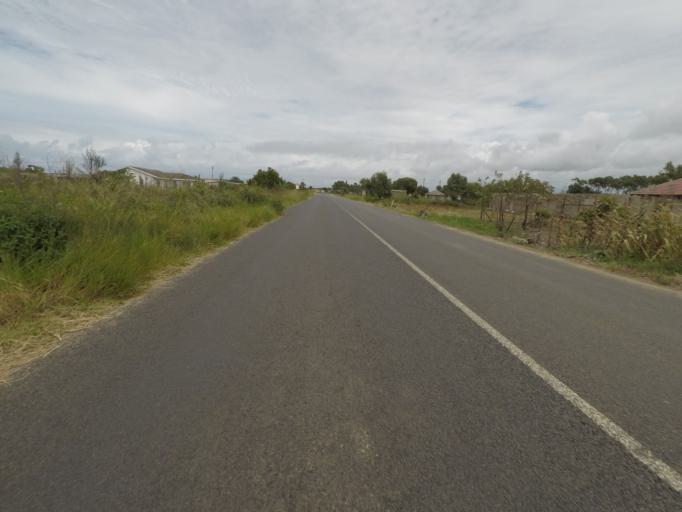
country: ZA
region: KwaZulu-Natal
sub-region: uThungulu District Municipality
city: eSikhawini
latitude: -28.9055
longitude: 31.8846
